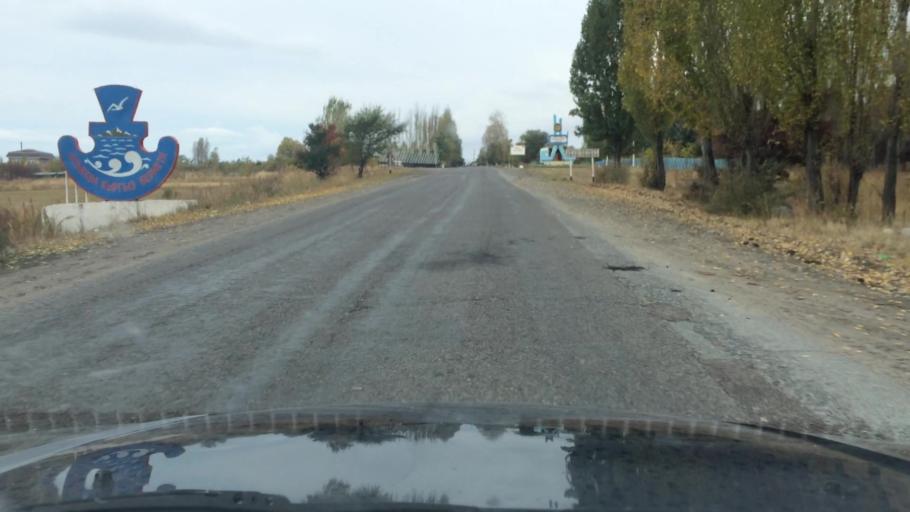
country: KG
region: Ysyk-Koel
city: Pokrovka
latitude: 42.7368
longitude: 77.9503
